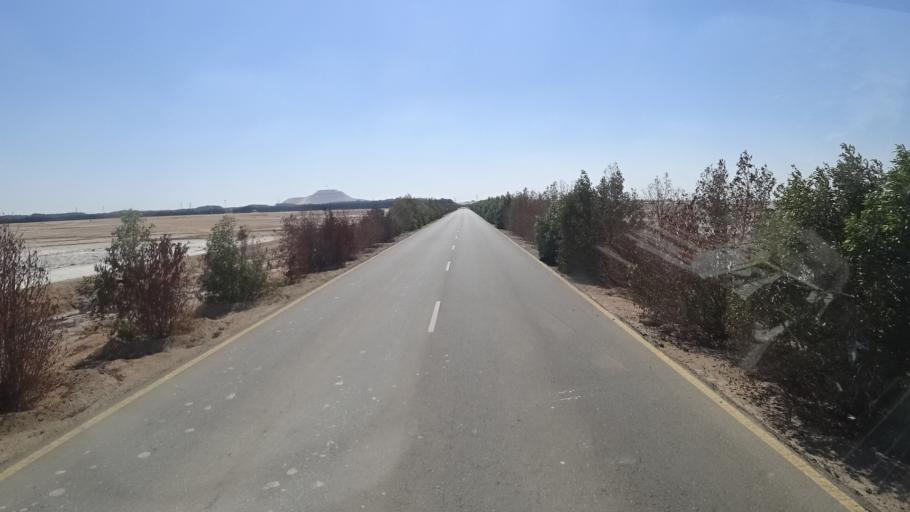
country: AE
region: Abu Dhabi
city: Abu Dhabi
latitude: 24.1956
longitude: 54.7009
